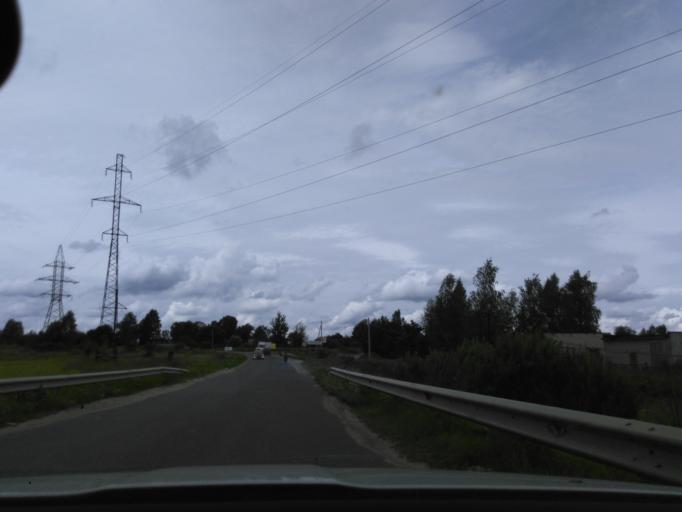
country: RU
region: Tverskaya
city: Konakovo
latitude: 56.6687
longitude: 36.7155
